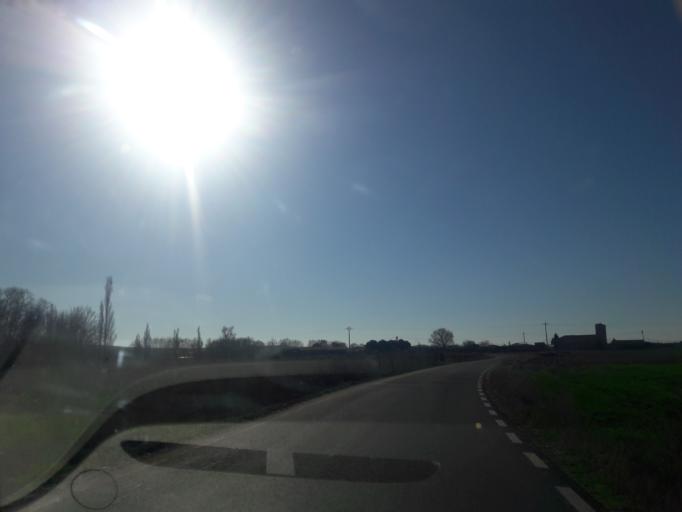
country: ES
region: Castille and Leon
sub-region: Provincia de Salamanca
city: Tordillos
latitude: 40.8581
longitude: -5.3568
